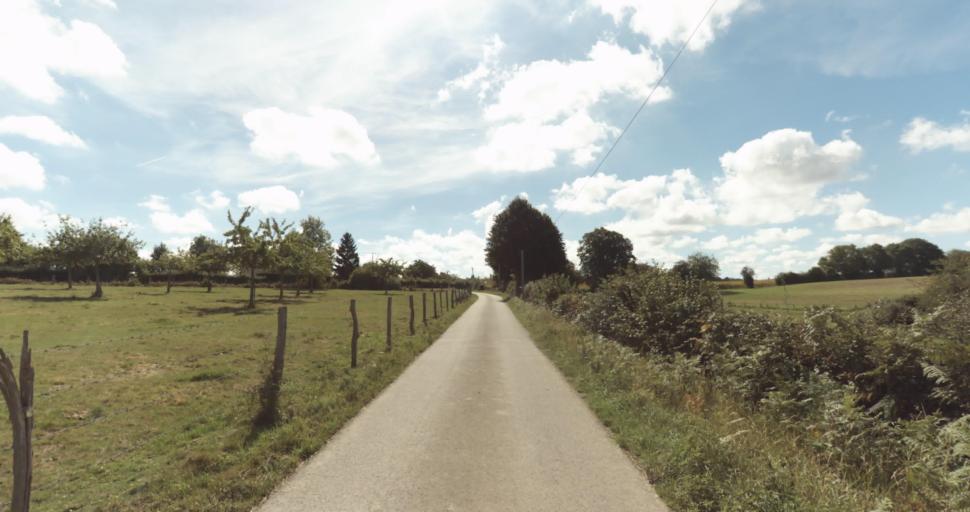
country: FR
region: Lower Normandy
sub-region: Departement du Calvados
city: Orbec
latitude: 48.9458
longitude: 0.3897
